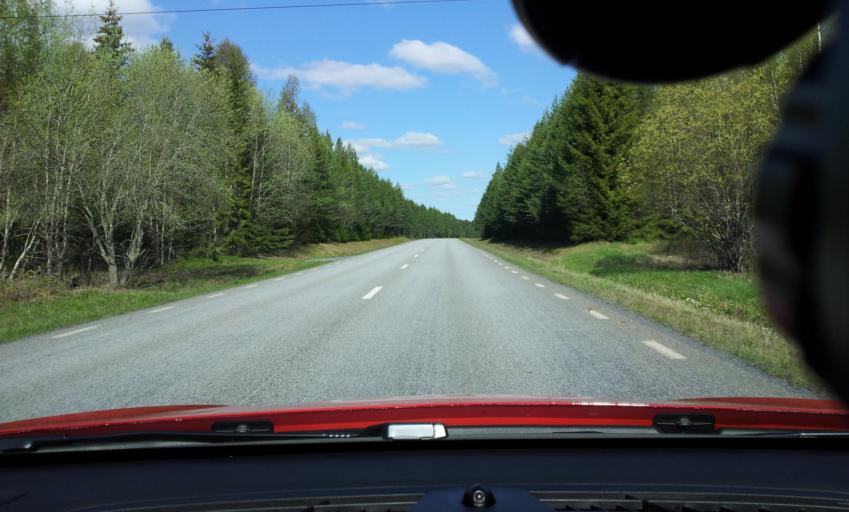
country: SE
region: Jaemtland
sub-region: Krokoms Kommun
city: Valla
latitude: 63.2708
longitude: 13.9531
